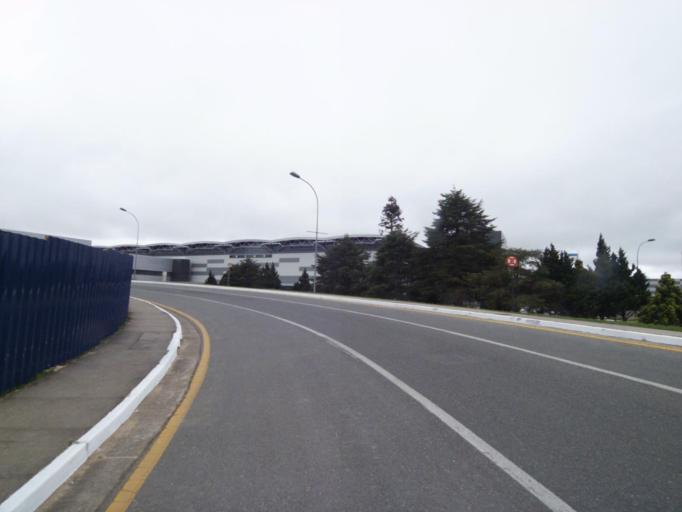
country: BR
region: Parana
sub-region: Sao Jose Dos Pinhais
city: Sao Jose dos Pinhais
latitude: -25.5380
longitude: -49.1730
